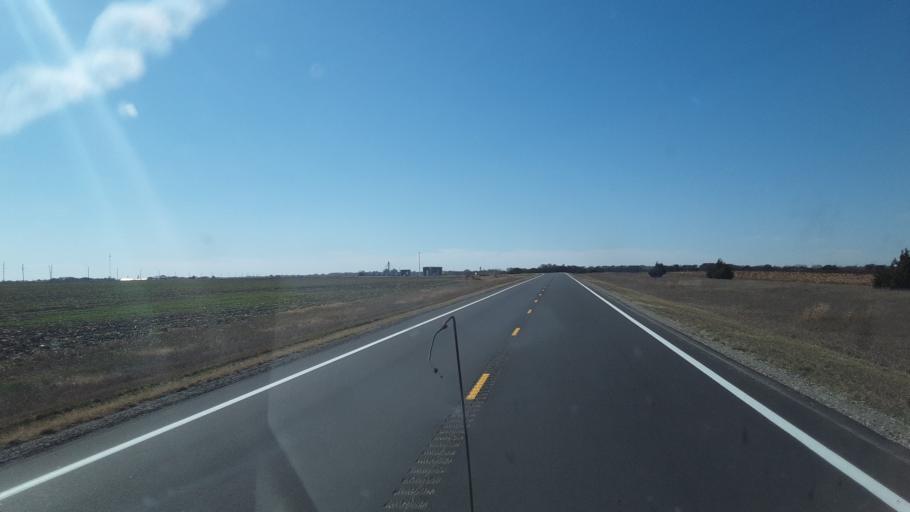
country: US
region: Kansas
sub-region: Rice County
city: Lyons
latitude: 38.3658
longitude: -98.1577
